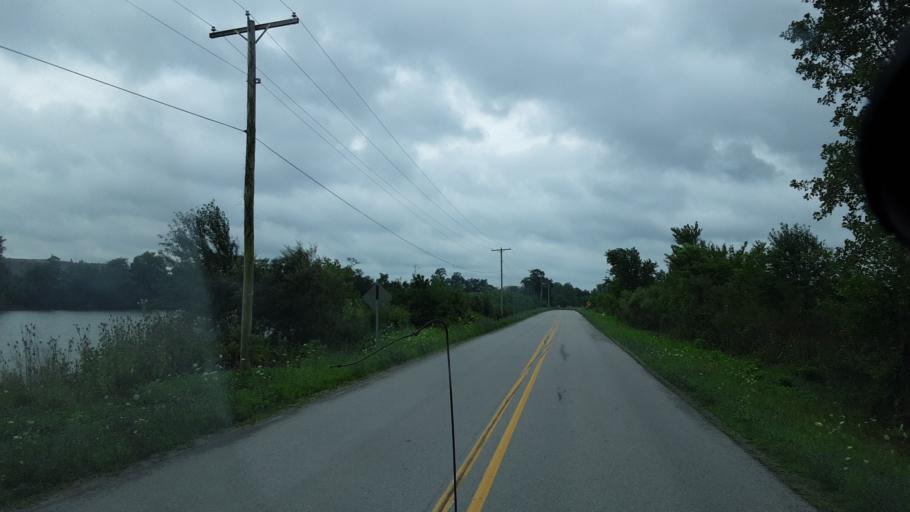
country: US
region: Indiana
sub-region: Wells County
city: Ossian
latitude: 40.9460
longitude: -85.0610
